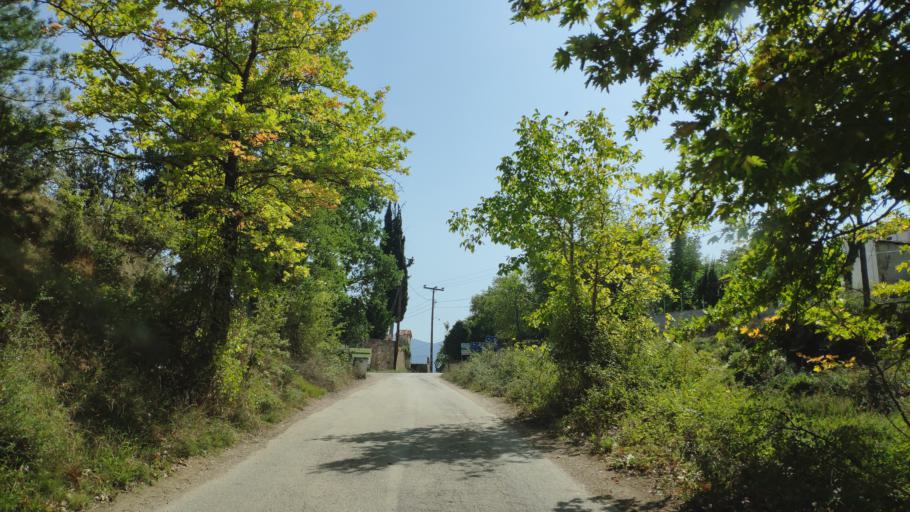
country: GR
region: West Greece
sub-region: Nomos Achaias
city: Kalavryta
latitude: 37.9215
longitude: 22.2952
